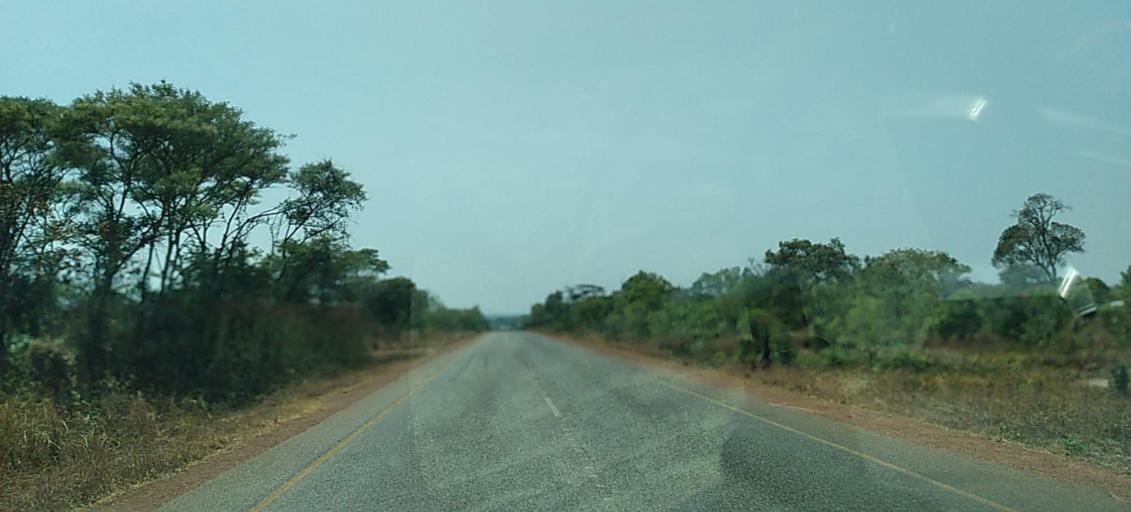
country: ZM
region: North-Western
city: Solwezi
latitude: -12.3940
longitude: 26.2230
